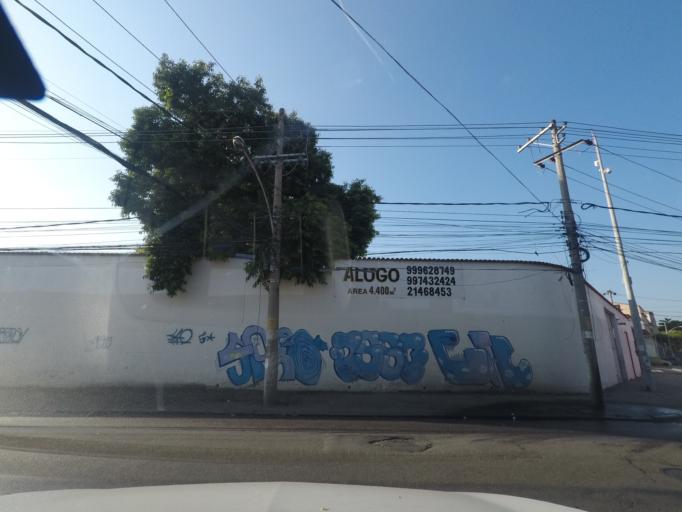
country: BR
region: Rio de Janeiro
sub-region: Rio De Janeiro
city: Rio de Janeiro
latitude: -22.8457
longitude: -43.2572
